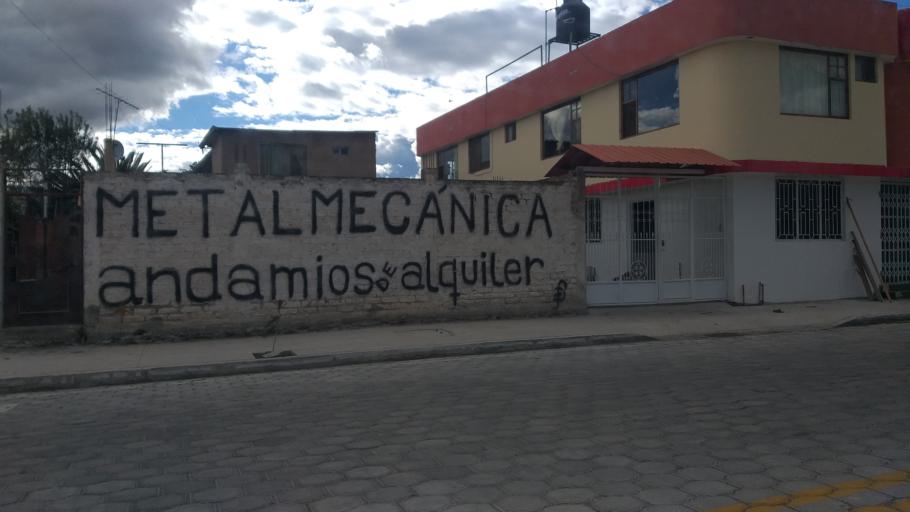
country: EC
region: Chimborazo
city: Riobamba
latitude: -1.6911
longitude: -78.6265
